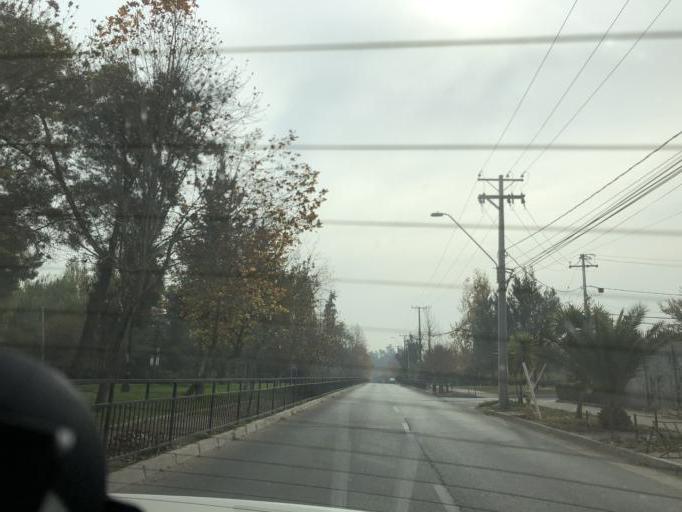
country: CL
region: Santiago Metropolitan
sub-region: Provincia de Cordillera
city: Puente Alto
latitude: -33.5555
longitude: -70.5530
